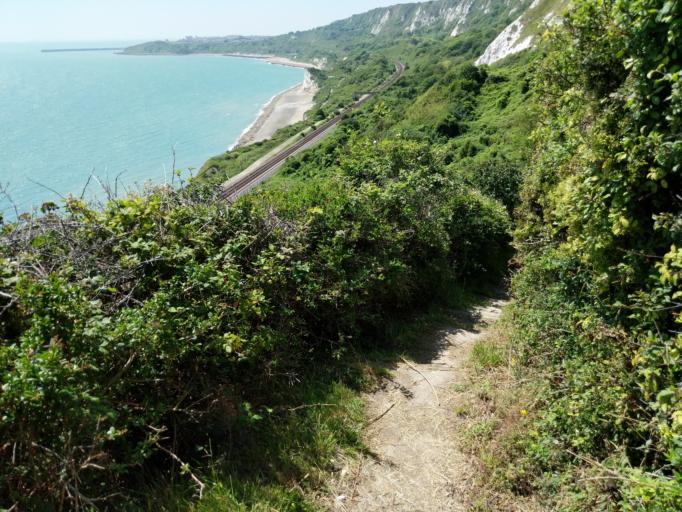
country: GB
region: England
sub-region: Kent
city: Folkestone
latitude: 51.1012
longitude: 1.2314
